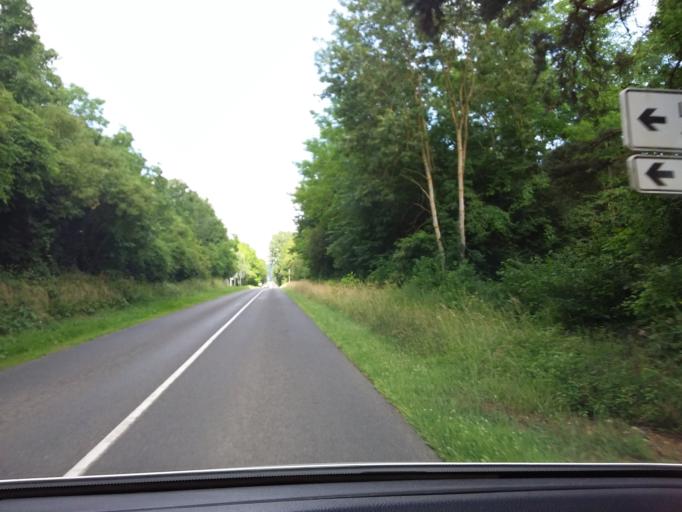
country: FR
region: Champagne-Ardenne
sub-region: Departement de la Marne
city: Fismes
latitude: 49.3787
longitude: 3.6560
